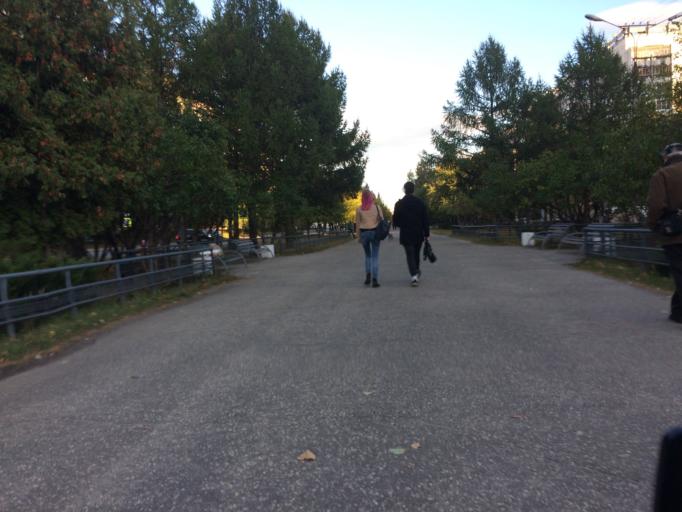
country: RU
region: Mariy-El
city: Yoshkar-Ola
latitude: 56.6319
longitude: 47.9119
